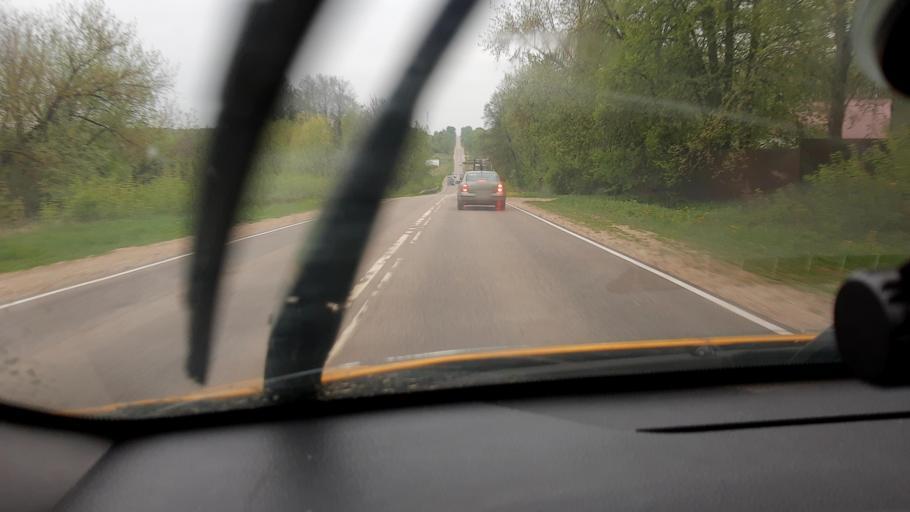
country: RU
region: Tula
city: Zaokskiy
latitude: 54.7841
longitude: 37.4341
